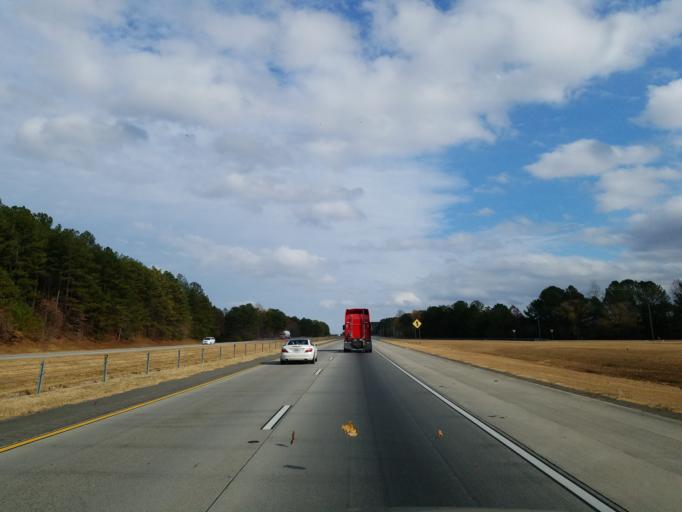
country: US
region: Georgia
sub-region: Haralson County
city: Tallapoosa
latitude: 33.6787
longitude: -85.3197
